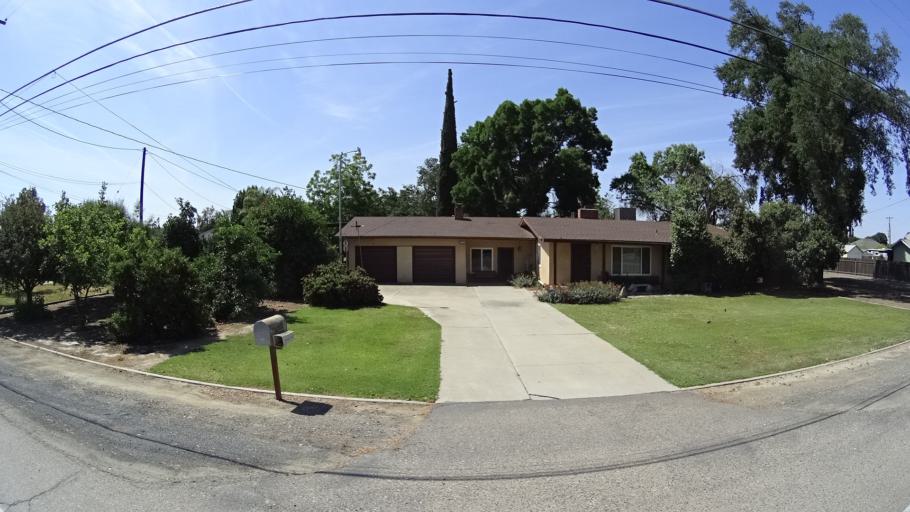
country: US
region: California
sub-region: Kings County
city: Armona
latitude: 36.3426
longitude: -119.7072
